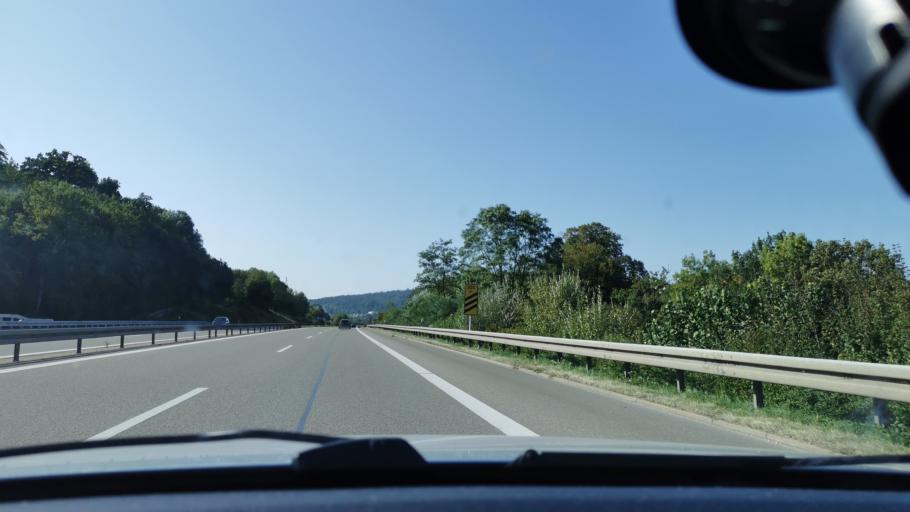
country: DE
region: Baden-Wuerttemberg
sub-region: Regierungsbezirk Stuttgart
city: Albershausen
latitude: 48.7109
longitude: 9.5663
